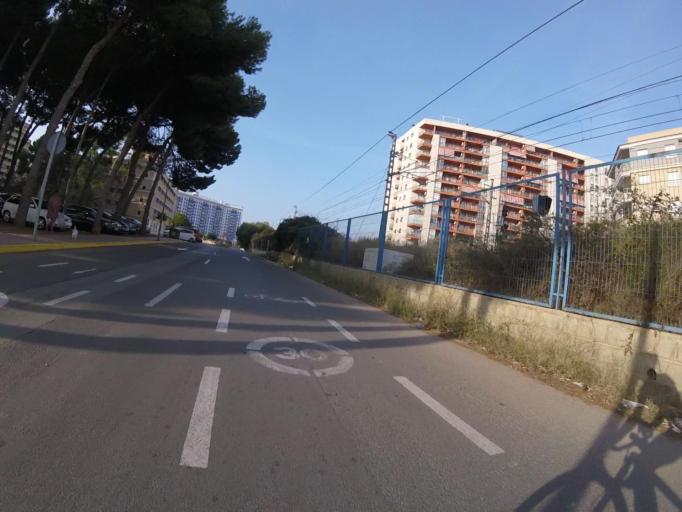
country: ES
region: Valencia
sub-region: Provincia de Castello
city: Orpesa/Oropesa del Mar
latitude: 40.0887
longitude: 0.1389
